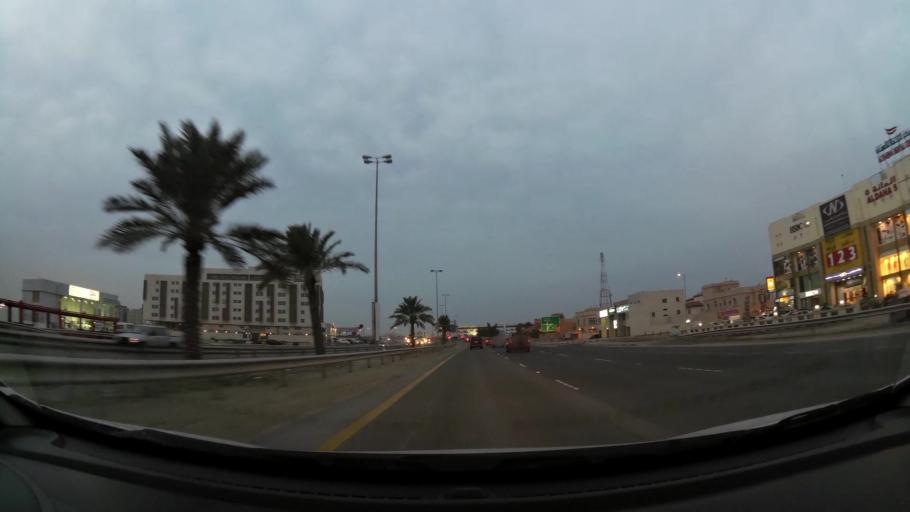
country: BH
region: Northern
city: Ar Rifa'
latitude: 26.1472
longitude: 50.5766
